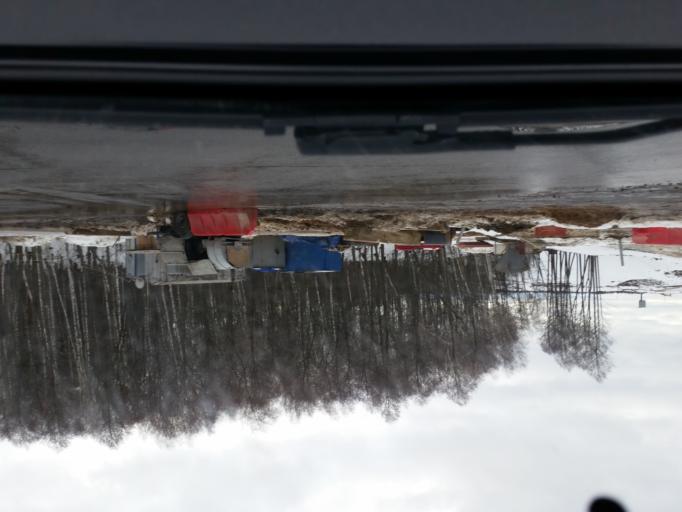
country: RU
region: Moskovskaya
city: Shcherbinka
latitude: 55.5254
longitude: 37.6004
